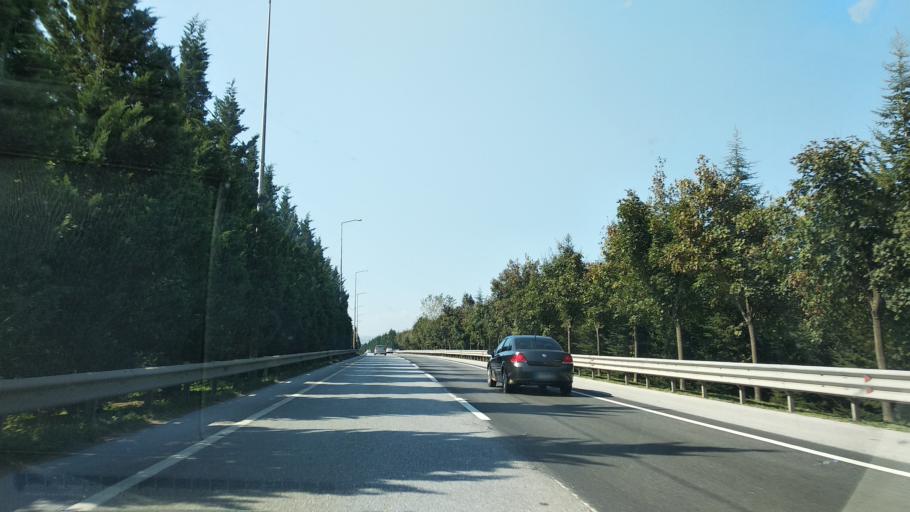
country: TR
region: Kocaeli
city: Kosekoy
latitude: 40.7552
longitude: 30.0115
